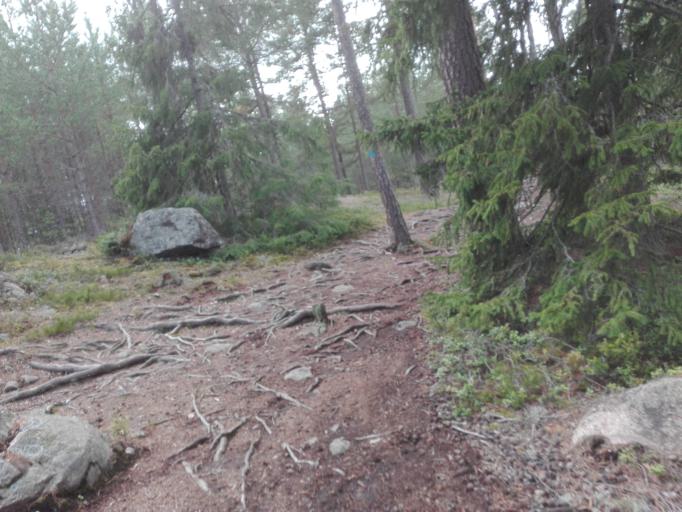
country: SE
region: Stockholm
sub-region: Tyreso Kommun
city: Bollmora
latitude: 59.2785
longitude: 18.2281
